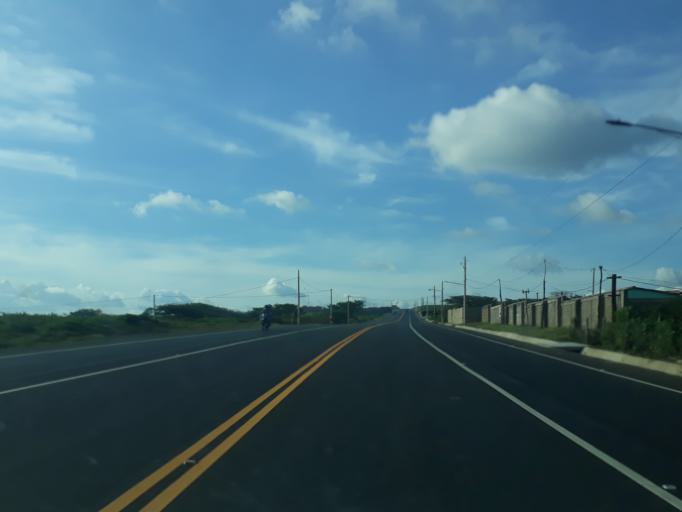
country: NI
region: Managua
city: El Crucero
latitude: 11.9474
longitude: -86.3000
